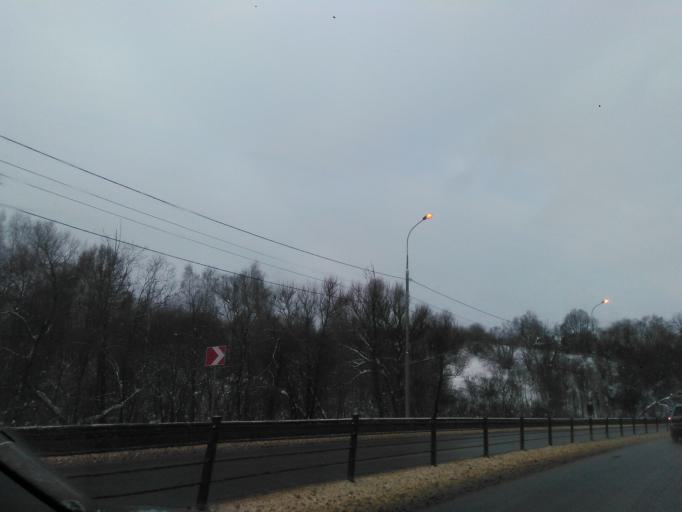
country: RU
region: Moskovskaya
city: Dedenevo
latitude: 56.2520
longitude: 37.5136
